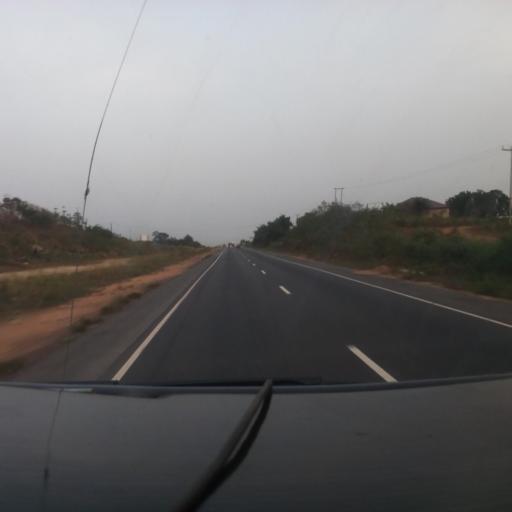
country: GH
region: Eastern
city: Nsawam
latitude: 5.8832
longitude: -0.3762
